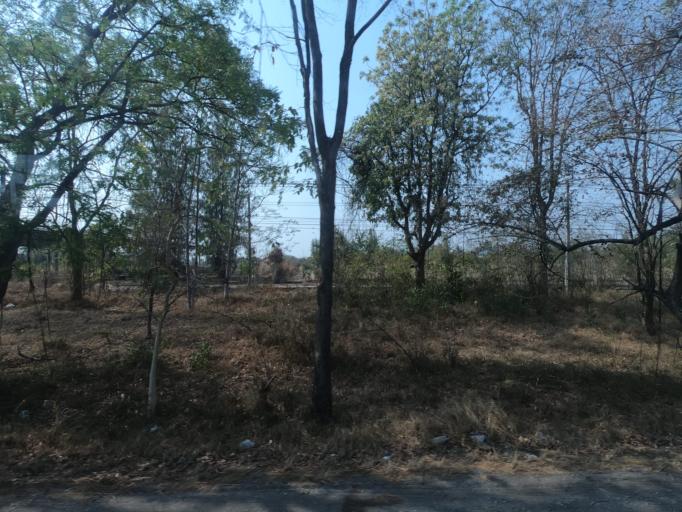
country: TH
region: Khon Kaen
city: Non Sila
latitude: 15.9102
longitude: 102.6575
